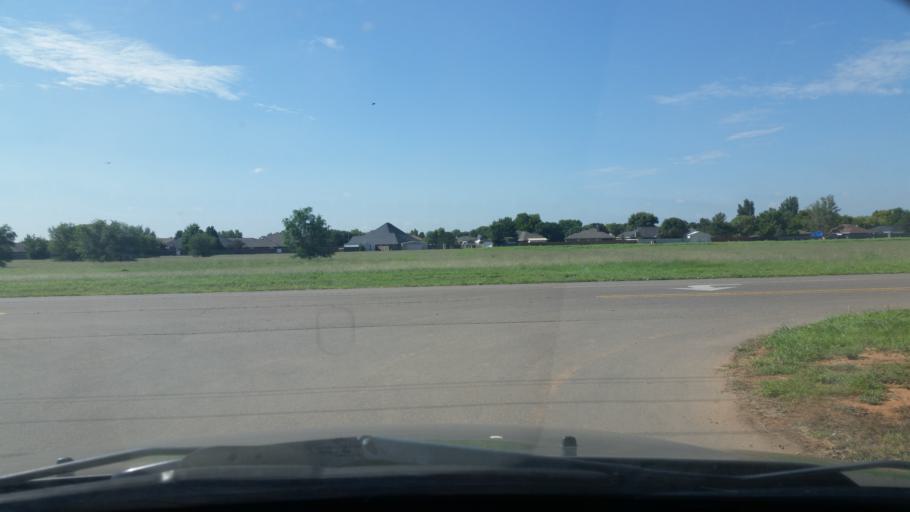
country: US
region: New Mexico
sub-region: Curry County
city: Clovis
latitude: 34.4340
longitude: -103.1738
